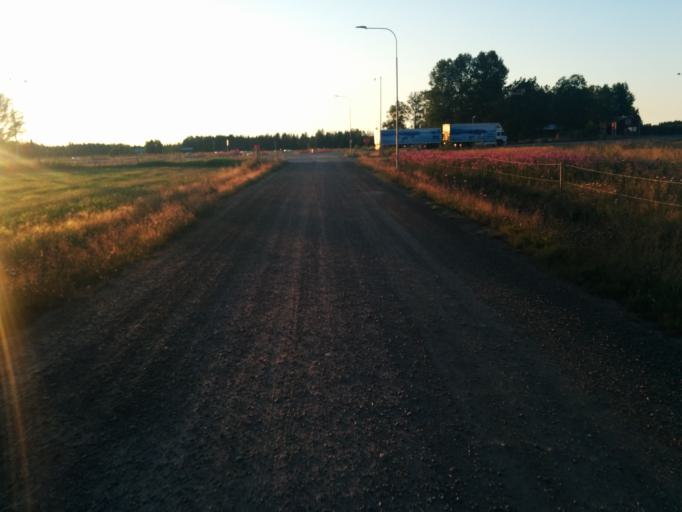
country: SE
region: Vaesterbotten
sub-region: Umea Kommun
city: Ersmark
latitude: 63.8548
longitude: 20.3884
